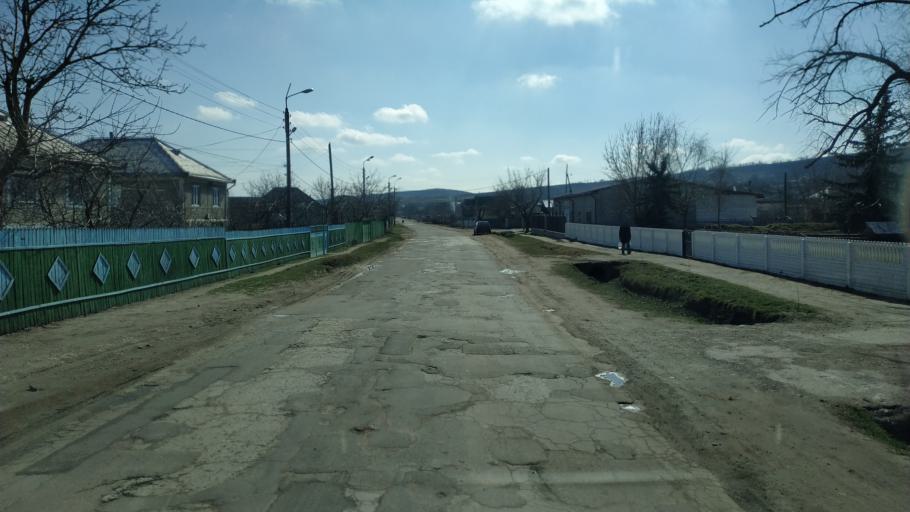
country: MD
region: Hincesti
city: Hincesti
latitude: 46.9608
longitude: 28.6030
